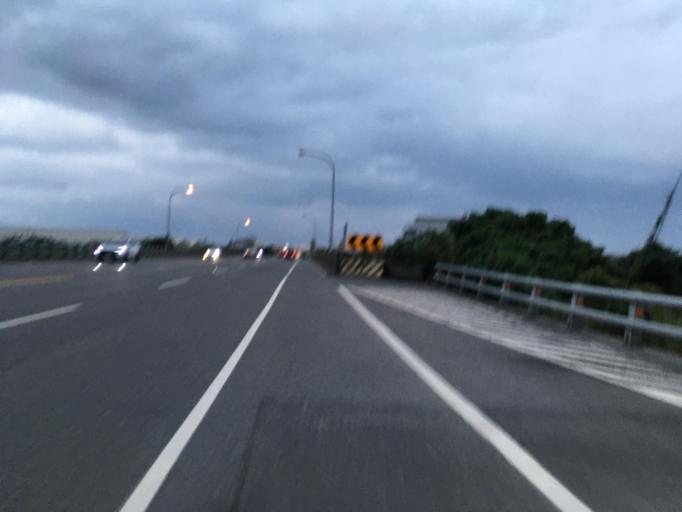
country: TW
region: Taiwan
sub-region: Yilan
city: Yilan
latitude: 24.6309
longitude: 121.8320
